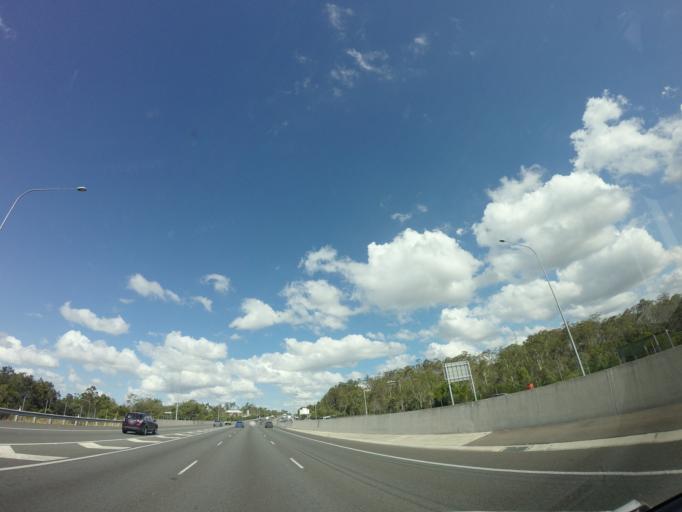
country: AU
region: Queensland
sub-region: Ipswich
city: Redbank
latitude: -27.6010
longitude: 152.8787
